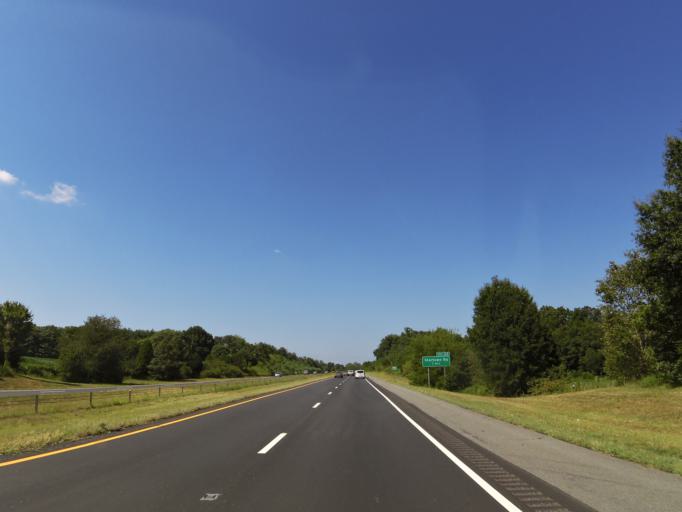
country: US
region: North Carolina
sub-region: Catawba County
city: Maiden
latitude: 35.5763
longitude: -81.2472
